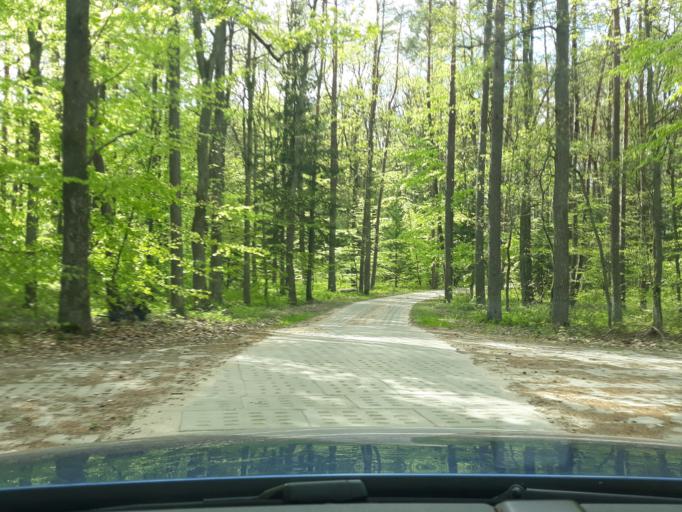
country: PL
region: Pomeranian Voivodeship
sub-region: Powiat czluchowski
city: Czluchow
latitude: 53.7459
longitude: 17.3358
